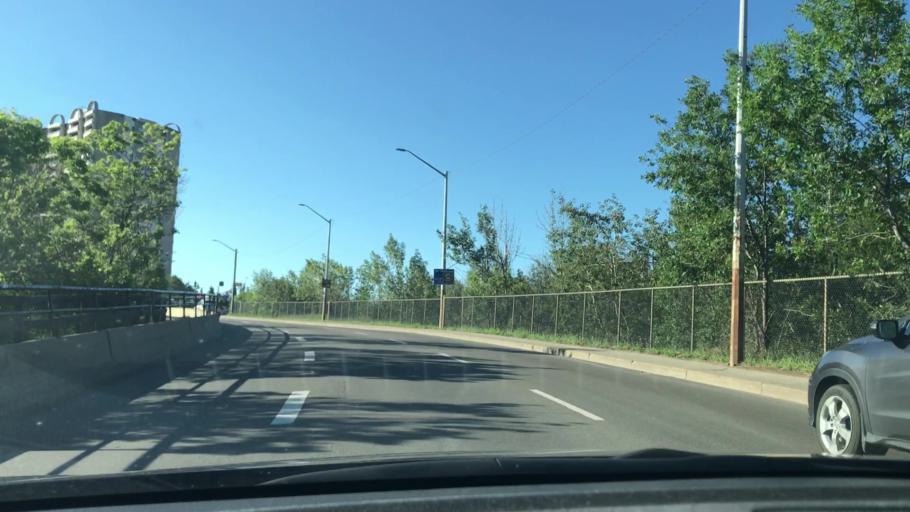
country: CA
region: Alberta
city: Edmonton
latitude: 53.5253
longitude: -113.5130
